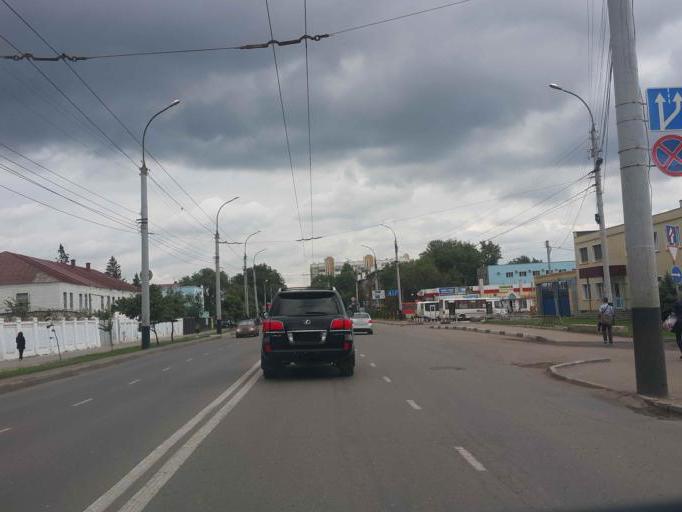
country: RU
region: Tambov
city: Tambov
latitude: 52.7380
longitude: 41.4376
